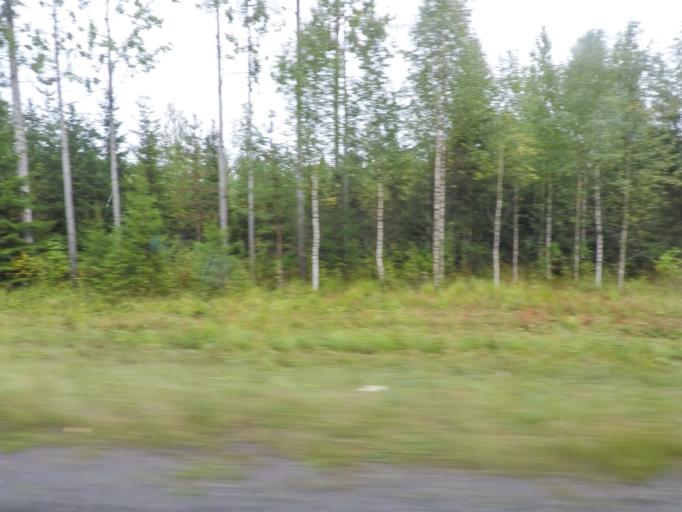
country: FI
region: Southern Savonia
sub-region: Pieksaemaeki
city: Juva
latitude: 61.9767
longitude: 27.8037
